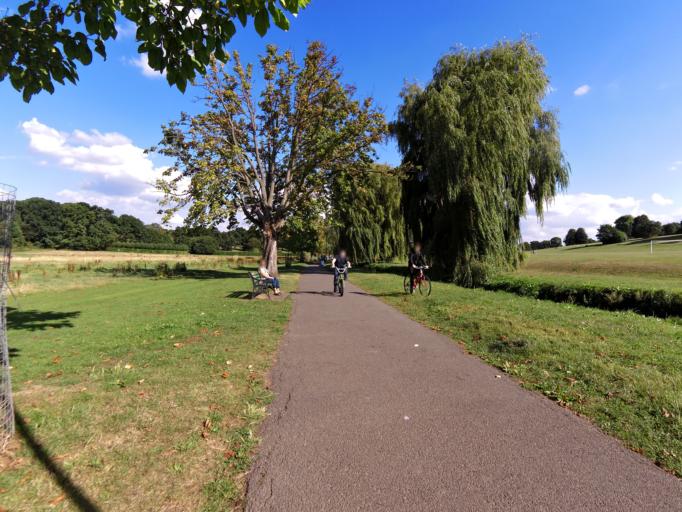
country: GB
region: England
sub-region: Greater London
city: Hadley Wood
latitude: 51.6384
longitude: -0.1563
